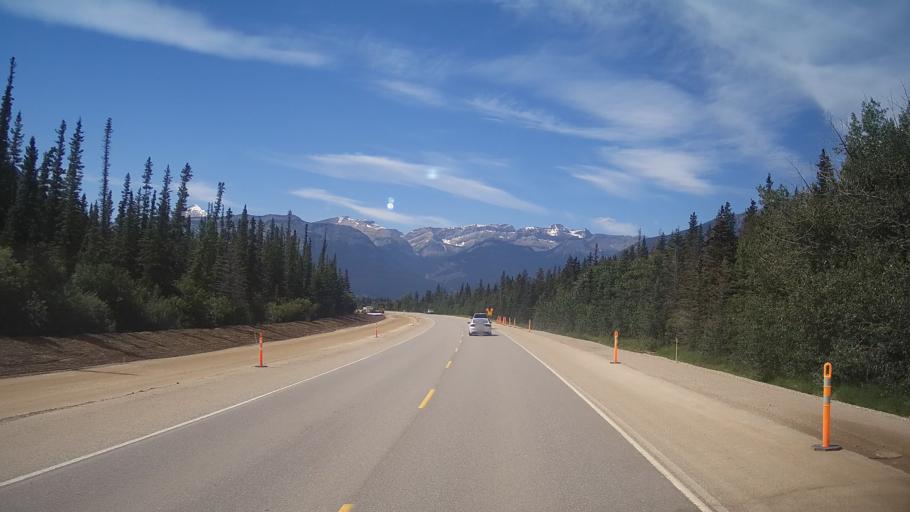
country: CA
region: Alberta
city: Jasper Park Lodge
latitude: 53.0686
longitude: -118.0589
